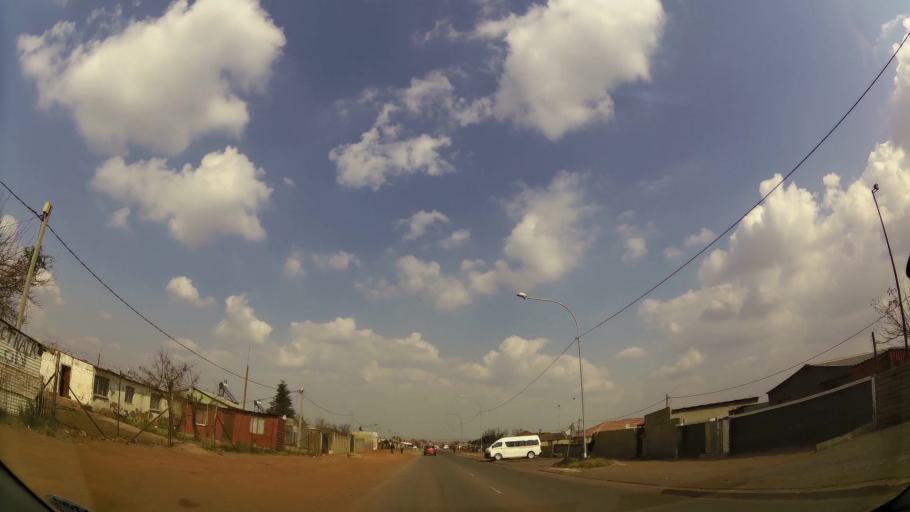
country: ZA
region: Gauteng
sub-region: Ekurhuleni Metropolitan Municipality
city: Springs
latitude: -26.1230
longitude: 28.4783
